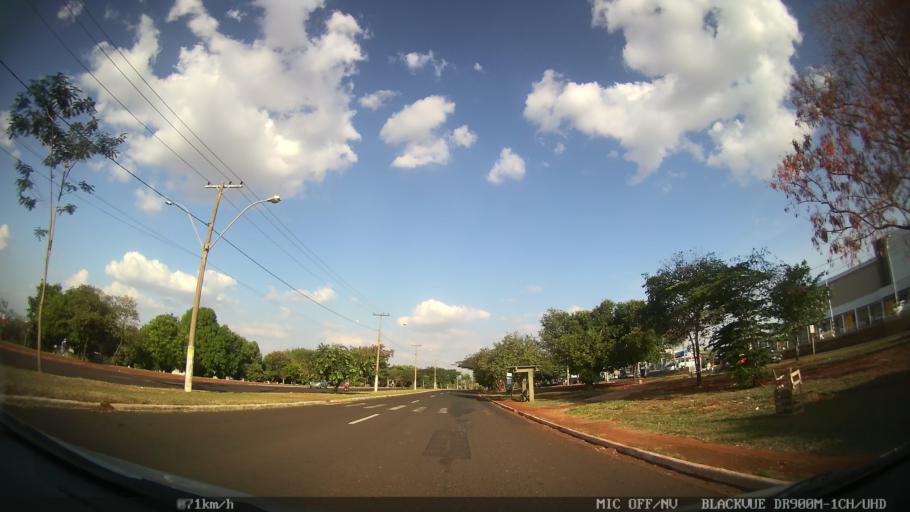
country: BR
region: Sao Paulo
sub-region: Ribeirao Preto
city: Ribeirao Preto
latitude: -21.1363
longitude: -47.8366
